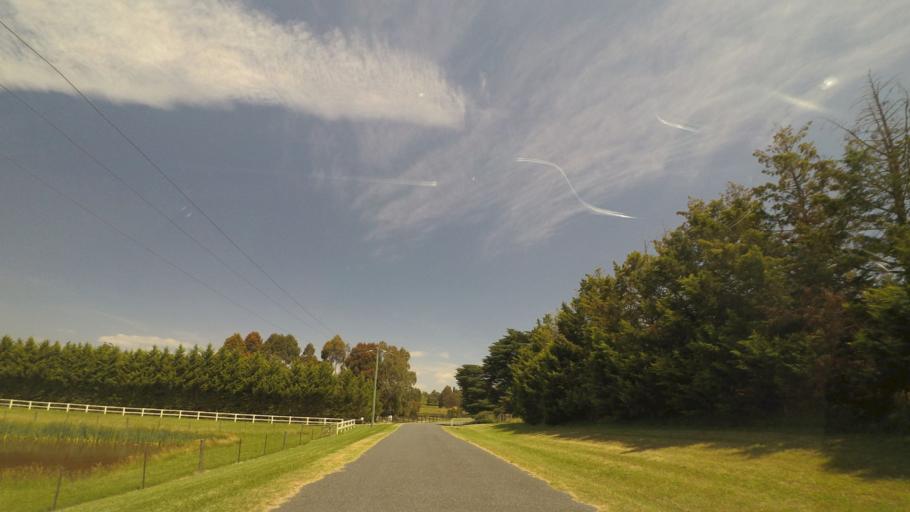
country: AU
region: Victoria
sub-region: Yarra Ranges
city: Chirnside Park
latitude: -37.7438
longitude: 145.3048
